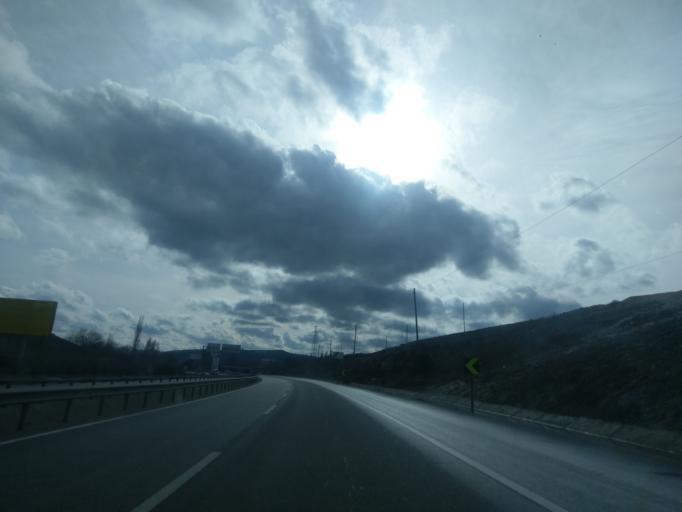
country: TR
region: Eskisehir
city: Inonu
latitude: 39.7060
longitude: 30.1552
